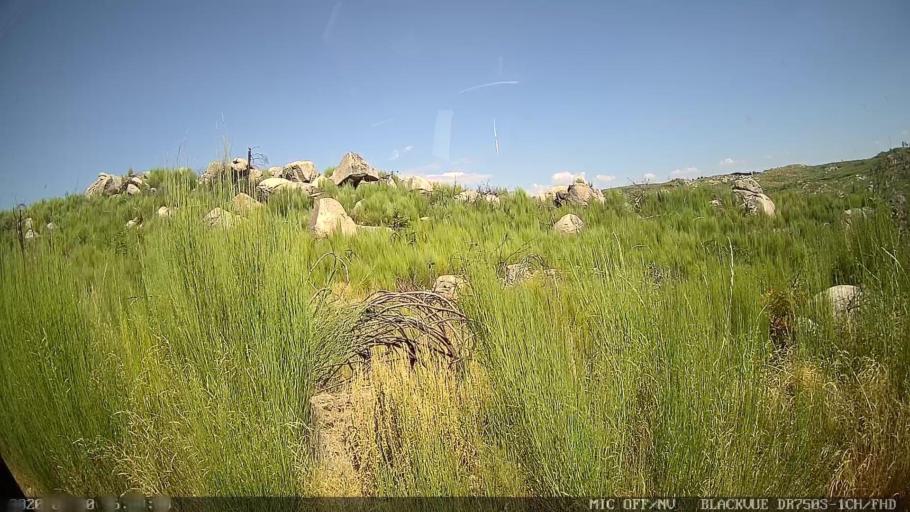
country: PT
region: Vila Real
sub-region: Sabrosa
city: Sabrosa
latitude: 41.3125
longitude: -7.4916
